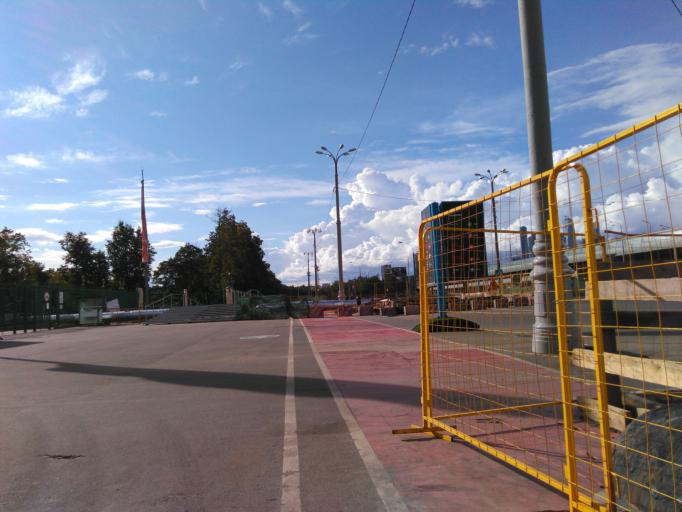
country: RU
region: Moscow
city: Luzhniki
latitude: 55.7214
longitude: 37.5537
